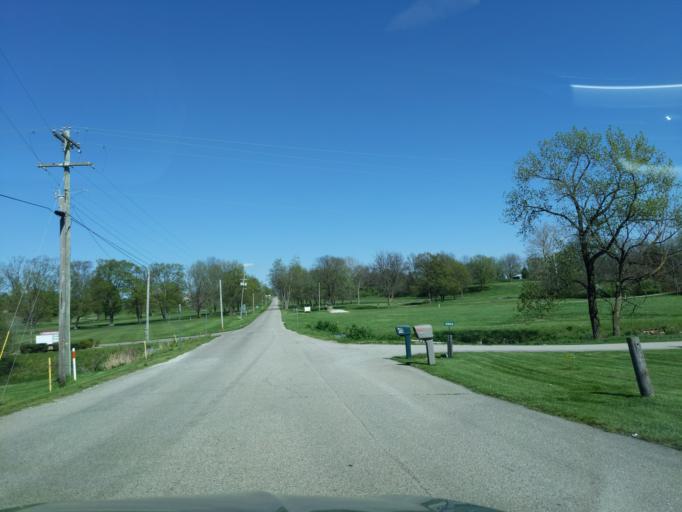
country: US
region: Indiana
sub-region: Decatur County
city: Greensburg
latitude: 39.3288
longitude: -85.5154
